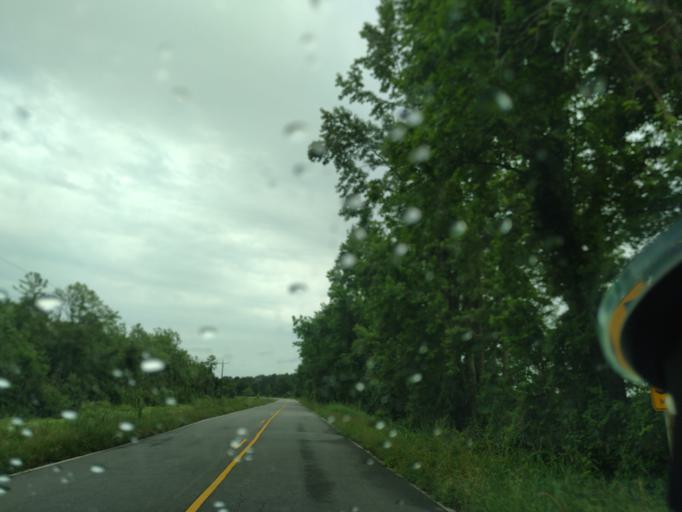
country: US
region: North Carolina
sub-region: Washington County
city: Plymouth
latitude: 35.7705
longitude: -76.5270
